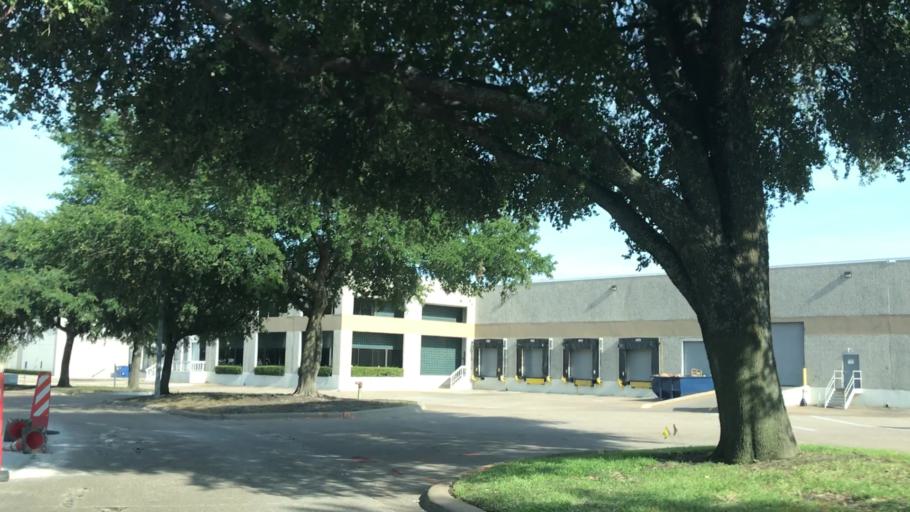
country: US
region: Texas
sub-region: Dallas County
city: Richardson
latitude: 32.8906
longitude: -96.7026
